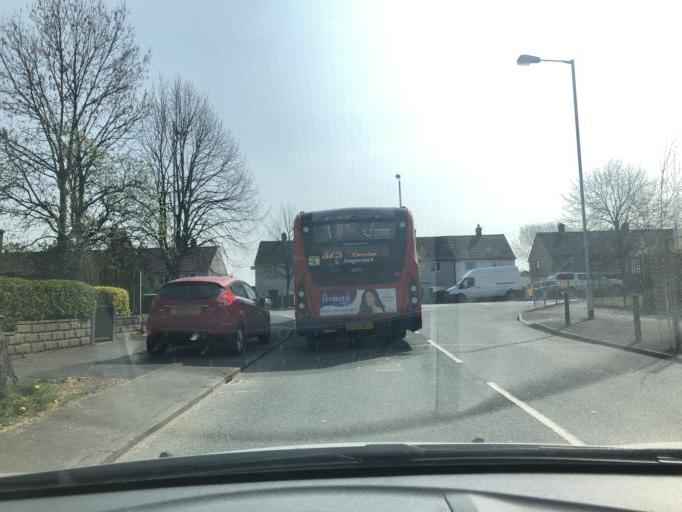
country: GB
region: England
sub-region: Borough of Stockport
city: Bredbury
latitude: 53.4287
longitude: -2.1296
